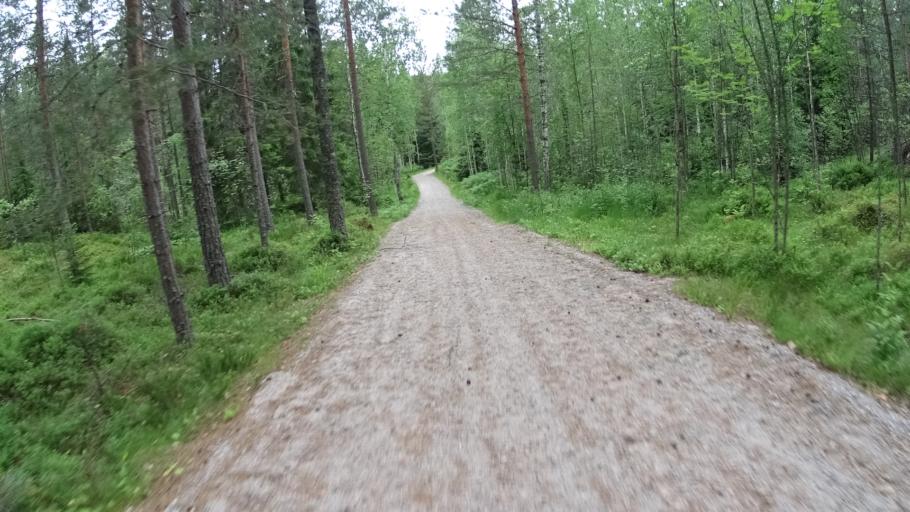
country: FI
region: Uusimaa
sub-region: Helsinki
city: Espoo
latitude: 60.2892
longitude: 24.5931
